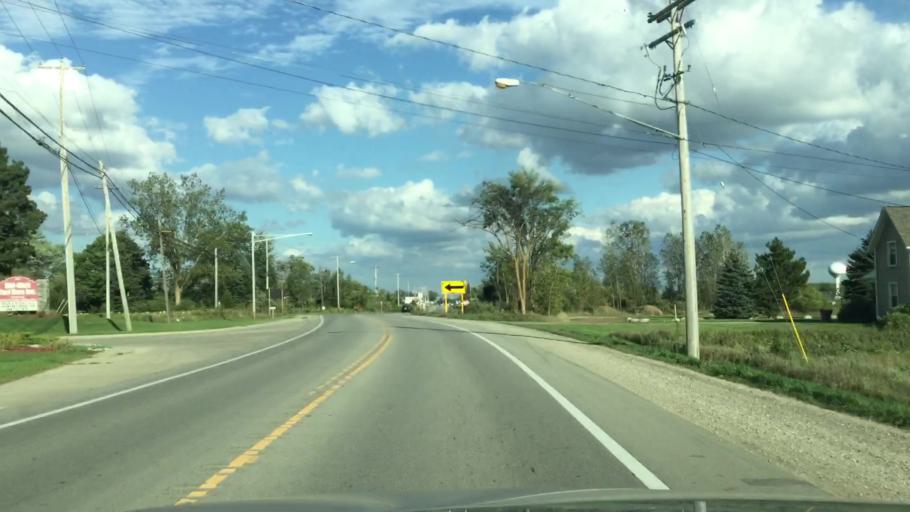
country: US
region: Michigan
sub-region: Shiawassee County
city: Owosso
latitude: 42.9977
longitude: -84.2164
